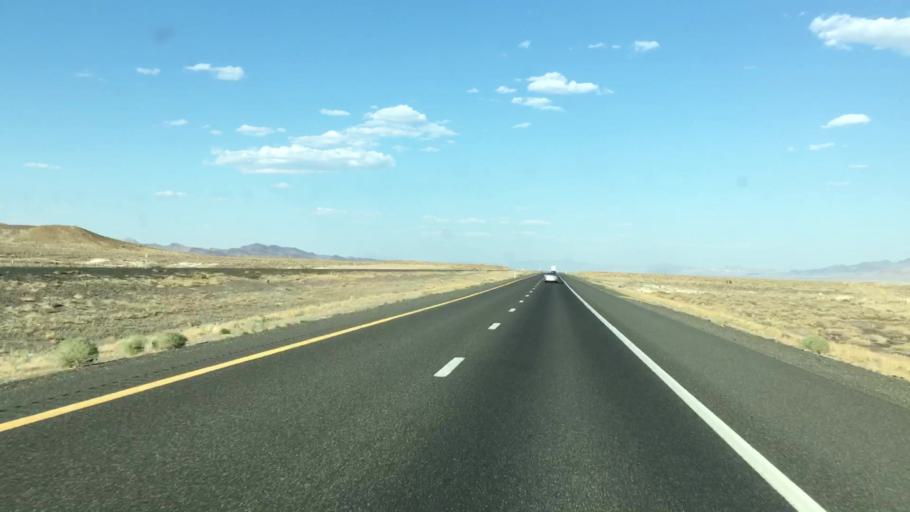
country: US
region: Nevada
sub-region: Churchill County
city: Fallon
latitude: 39.8638
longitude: -118.9028
